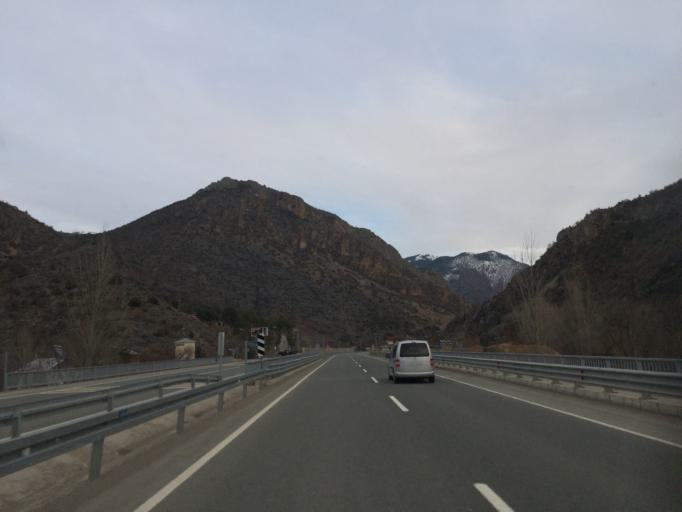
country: TR
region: Gumushane
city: Gumushkhane
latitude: 40.5247
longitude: 39.3924
